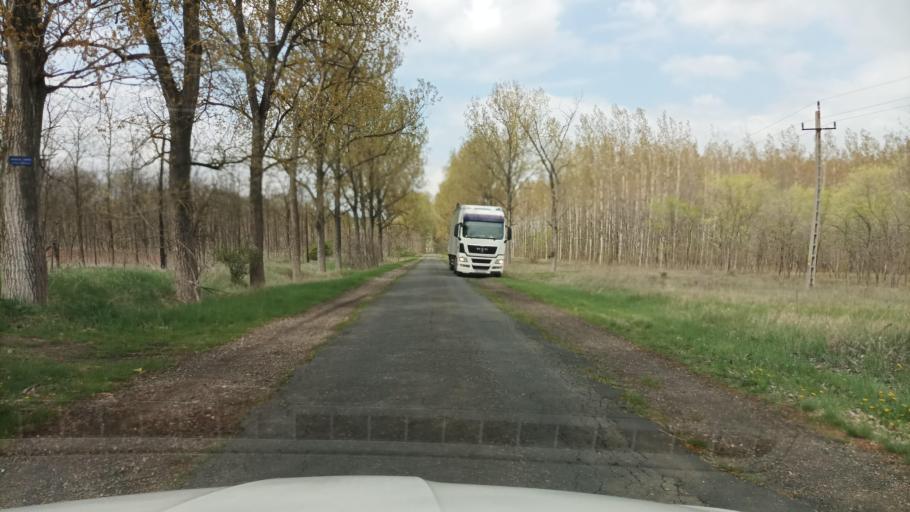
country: HU
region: Pest
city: Kocser
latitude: 47.0477
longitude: 19.9190
